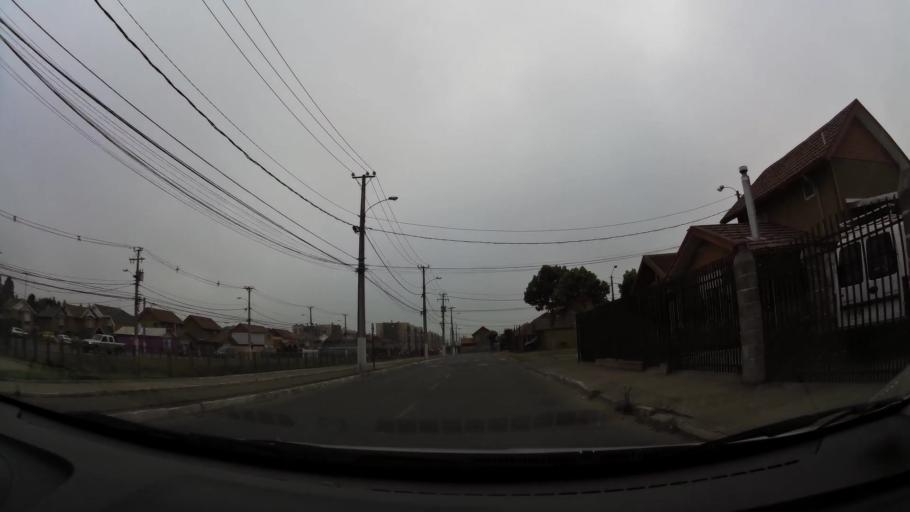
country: CL
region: Biobio
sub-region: Provincia de Concepcion
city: Concepcion
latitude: -36.7895
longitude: -73.0814
